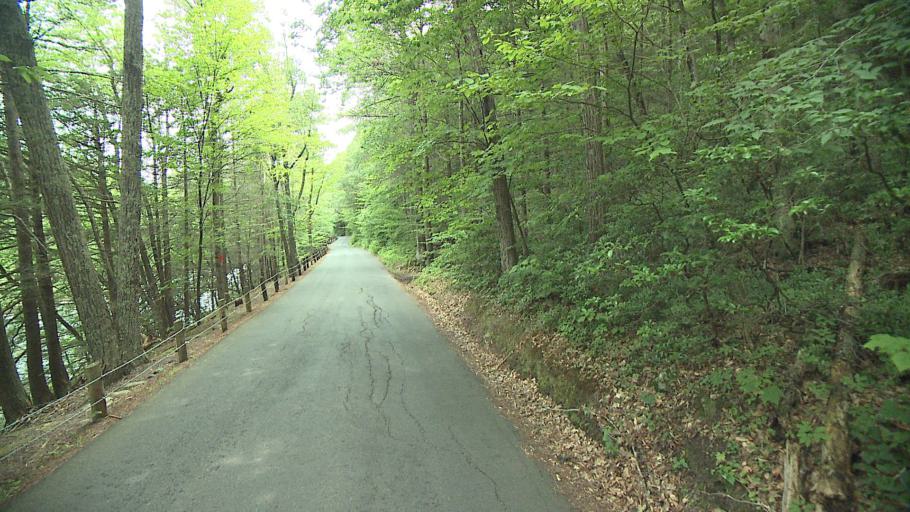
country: US
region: Connecticut
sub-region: Litchfield County
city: Winsted
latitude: 41.9499
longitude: -73.0134
